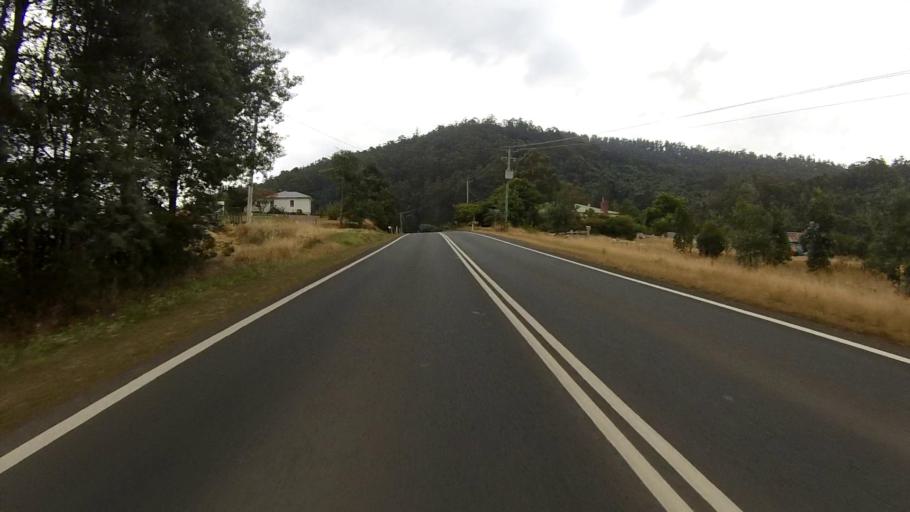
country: AU
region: Tasmania
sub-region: Huon Valley
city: Cygnet
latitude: -43.1429
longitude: 147.0640
